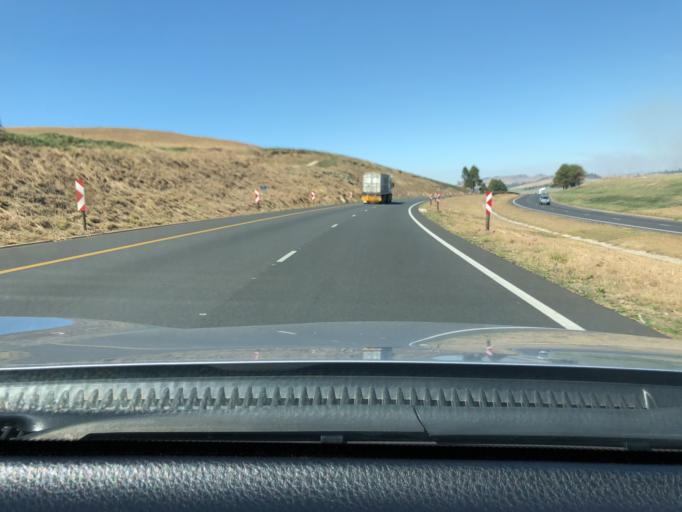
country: ZA
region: KwaZulu-Natal
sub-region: uMgungundlovu District Municipality
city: Mooirivier
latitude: -29.1610
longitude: 29.9826
